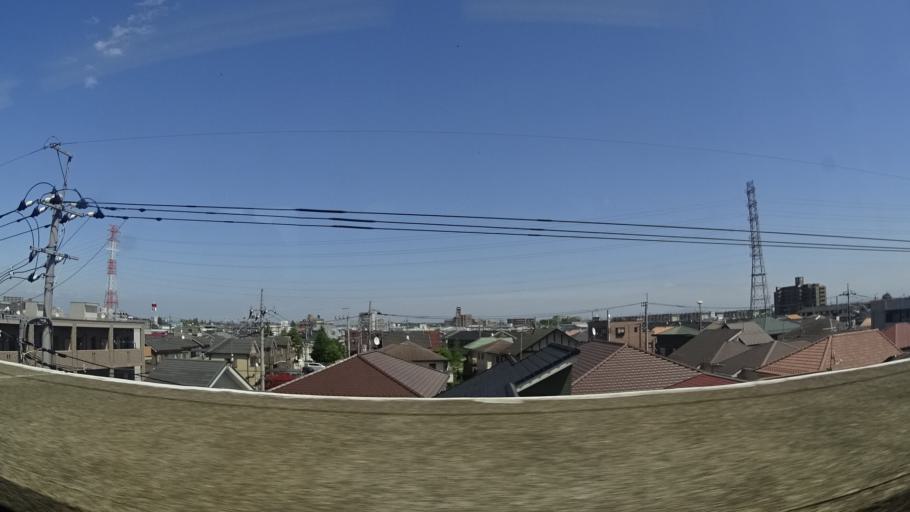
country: JP
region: Tochigi
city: Utsunomiya-shi
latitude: 36.5430
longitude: 139.8946
